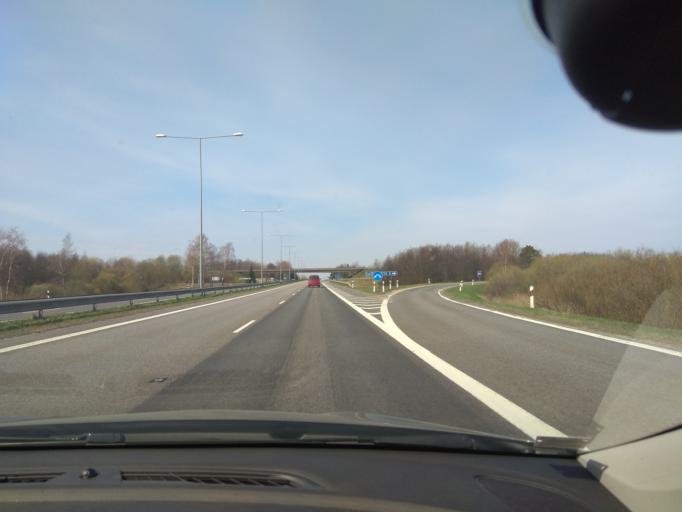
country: LT
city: Ziezmariai
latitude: 54.8172
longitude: 24.4322
